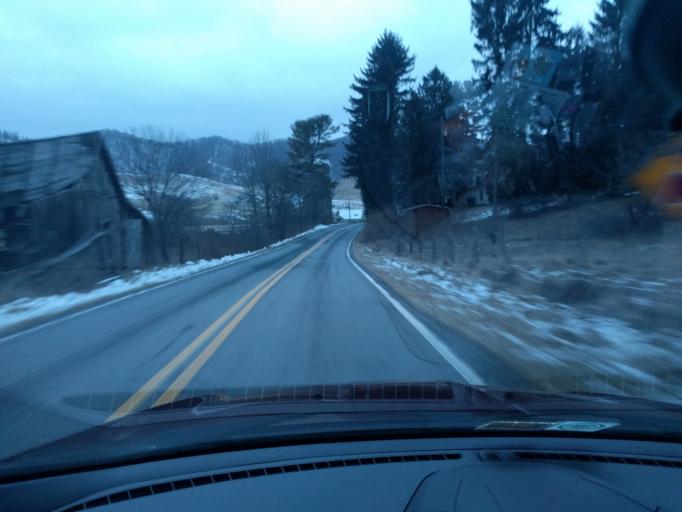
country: US
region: Virginia
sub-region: Alleghany County
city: Clifton Forge
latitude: 37.9041
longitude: -79.8976
